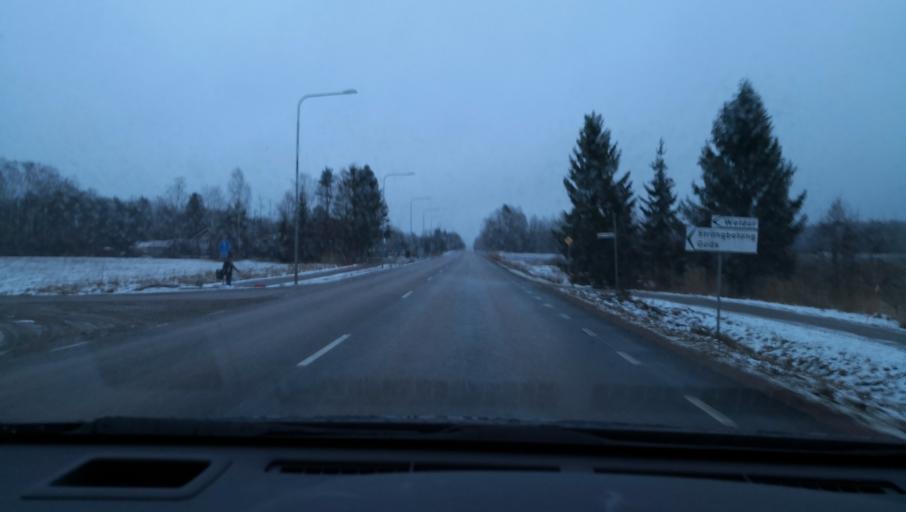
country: SE
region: Vaestmanland
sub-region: Kungsors Kommun
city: Kungsoer
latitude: 59.4234
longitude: 16.1351
